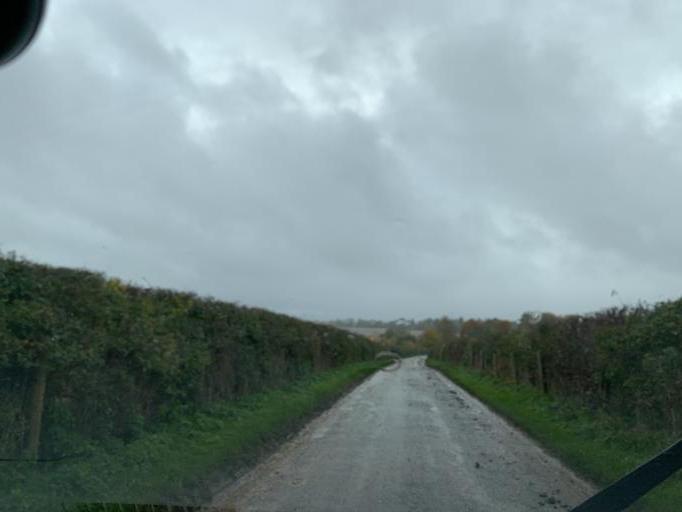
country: GB
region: England
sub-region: Wiltshire
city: Amesbury
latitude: 51.1515
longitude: -1.7853
